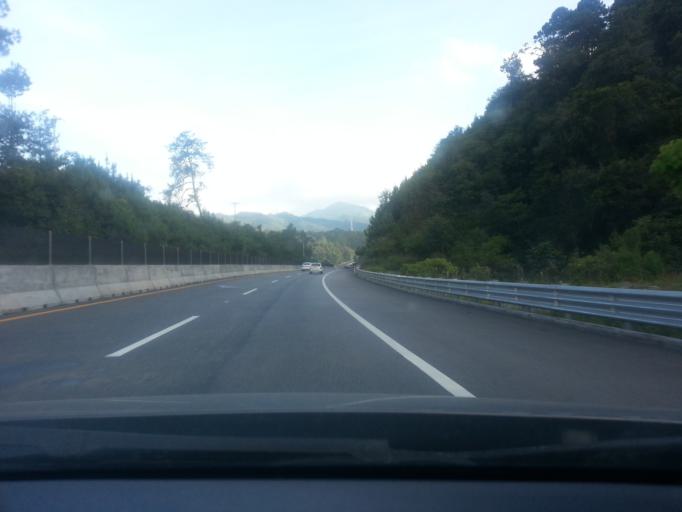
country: MX
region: Puebla
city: Necaxa
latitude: 20.2036
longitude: -98.0339
